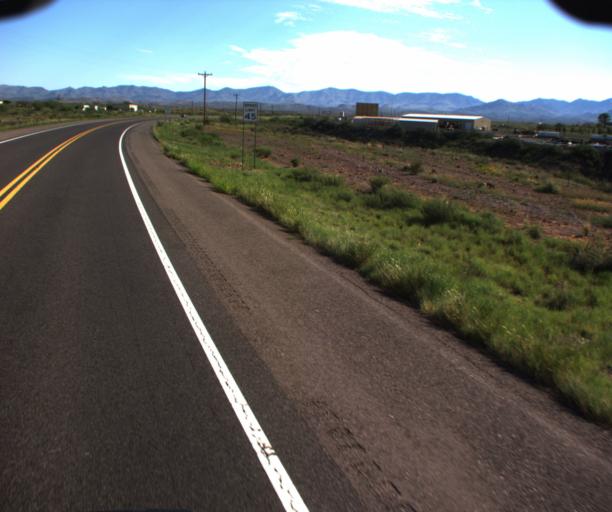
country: US
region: Arizona
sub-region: Greenlee County
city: Clifton
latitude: 32.9442
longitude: -109.2335
